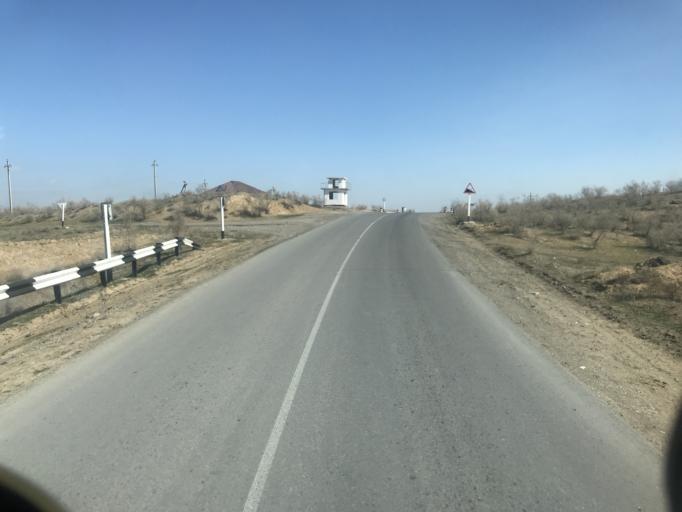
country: KZ
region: Ongtustik Qazaqstan
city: Shardara
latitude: 41.2509
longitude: 67.9047
